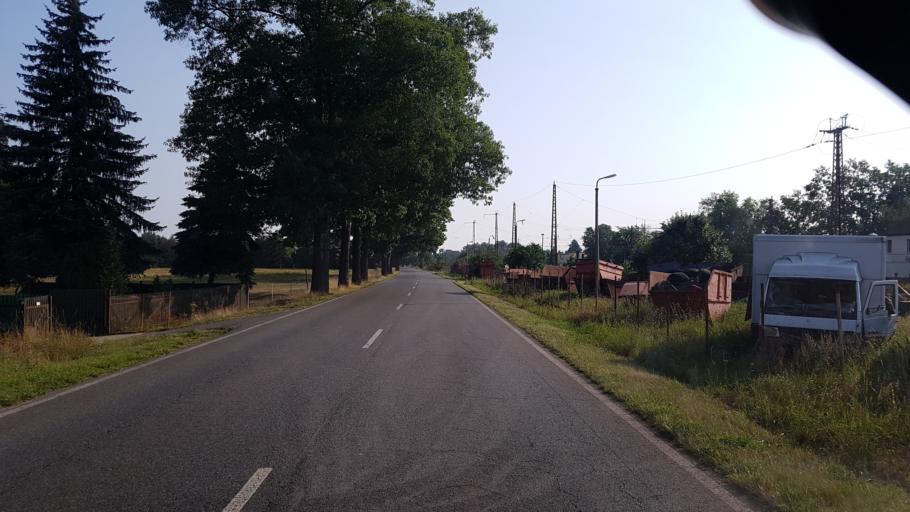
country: DE
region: Brandenburg
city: Drebkau
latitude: 51.6487
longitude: 14.2141
